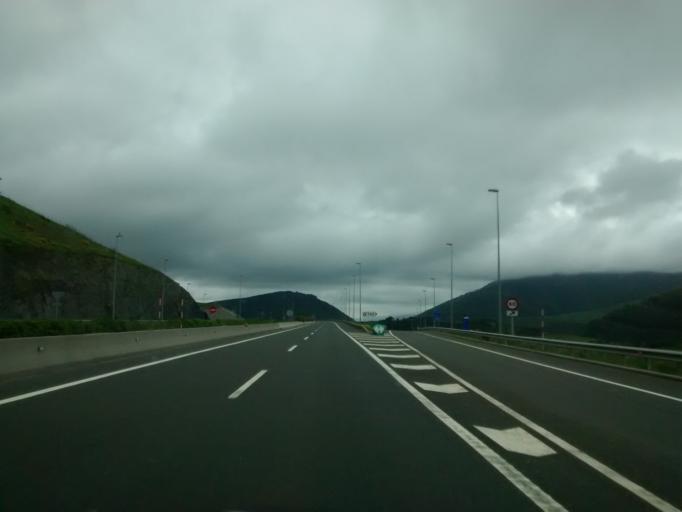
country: ES
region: Cantabria
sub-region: Provincia de Cantabria
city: Santiurde de Reinosa
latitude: 43.0643
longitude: -4.0894
